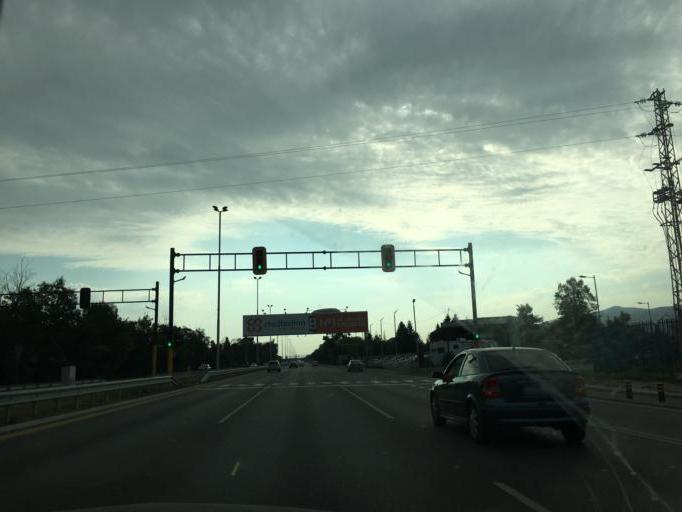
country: BG
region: Sofia-Capital
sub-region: Stolichna Obshtina
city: Sofia
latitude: 42.6347
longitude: 23.4357
